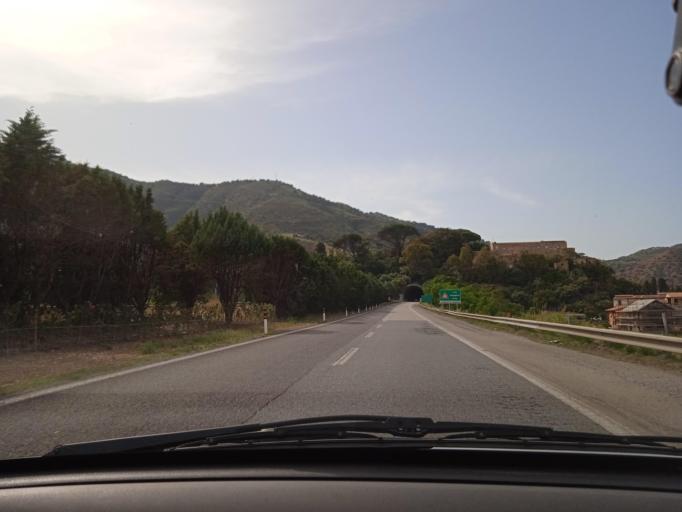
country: IT
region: Sicily
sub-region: Messina
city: Oliveri
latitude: 38.1196
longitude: 15.0586
